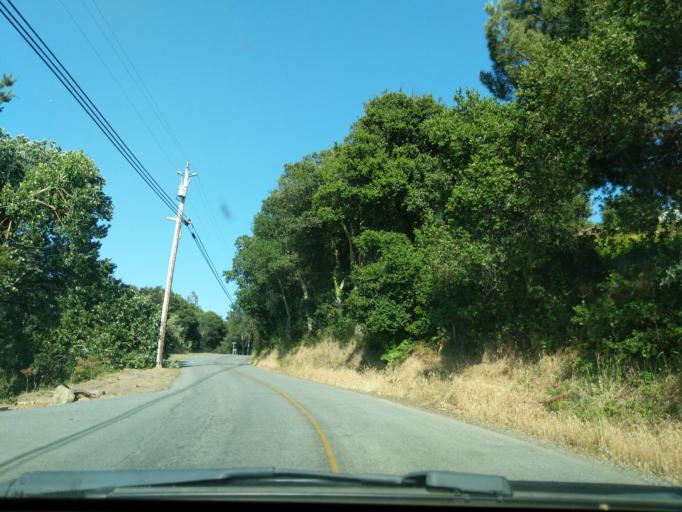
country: US
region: California
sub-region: Monterey County
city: Prunedale
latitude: 36.8017
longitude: -121.6338
